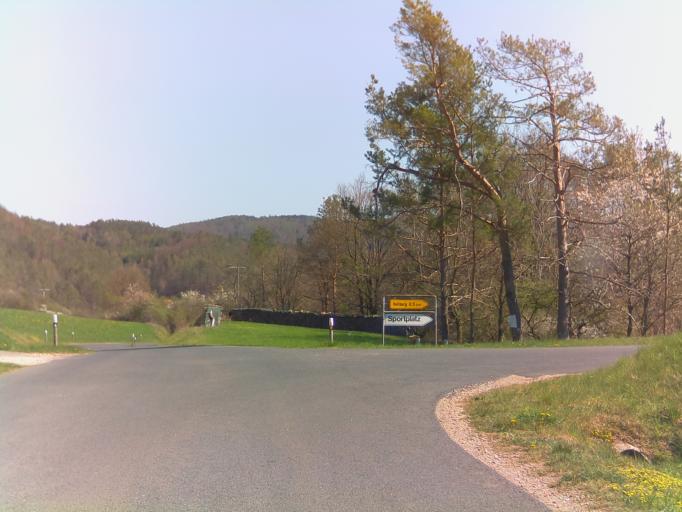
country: DE
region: Bavaria
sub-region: Upper Palatinate
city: Weigendorf
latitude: 49.4937
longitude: 11.5981
